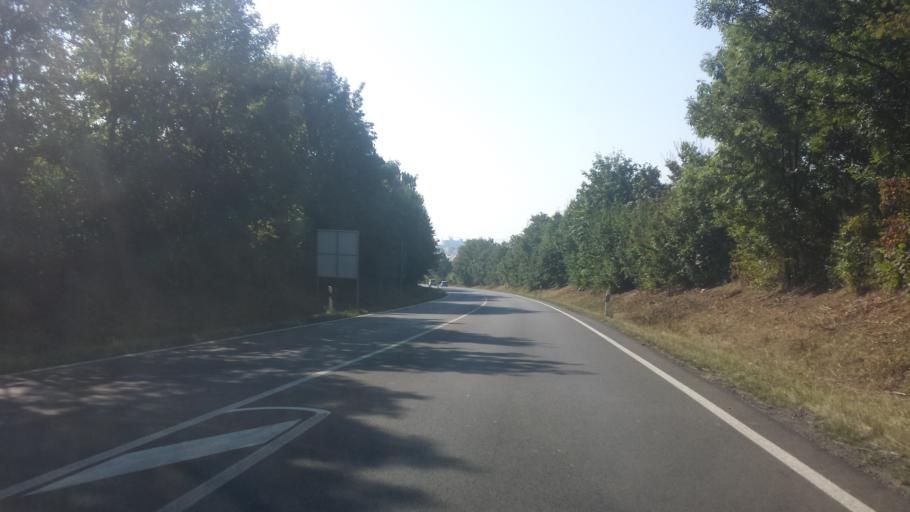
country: DE
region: Rheinland-Pfalz
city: Bockenheim
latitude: 49.5877
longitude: 8.1712
